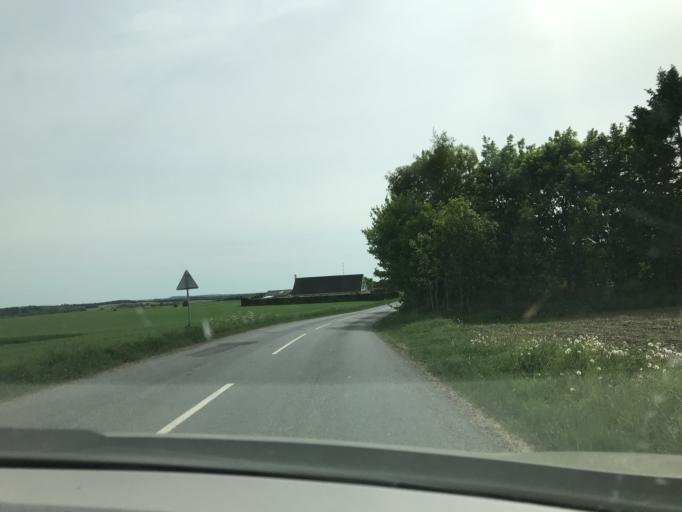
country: DK
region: Central Jutland
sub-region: Norddjurs Kommune
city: Allingabro
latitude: 56.5634
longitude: 10.3064
